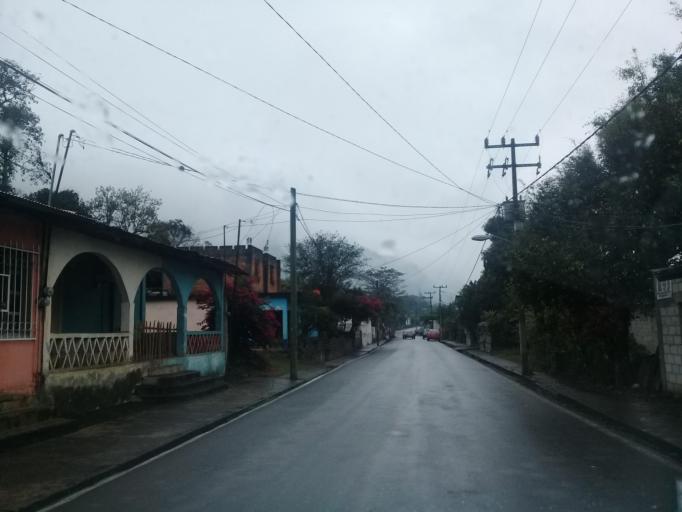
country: MX
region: Veracruz
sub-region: Amatlan de los Reyes
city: Centro de Readaptacion Social
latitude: 18.8073
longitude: -96.9578
